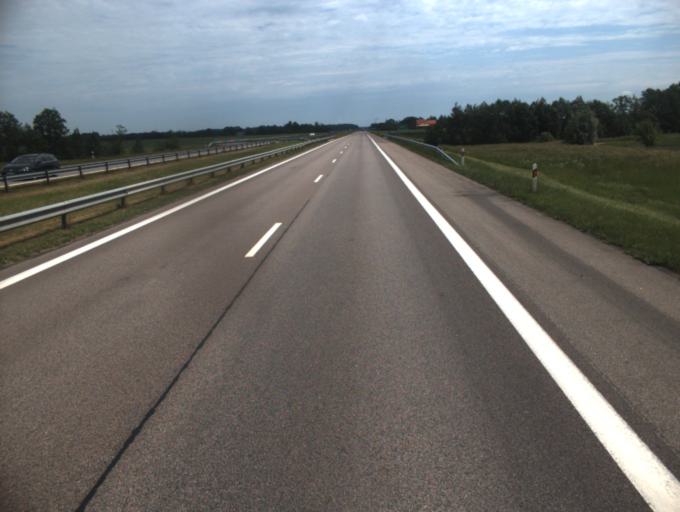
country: LT
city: Raseiniai
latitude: 55.3680
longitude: 22.9769
